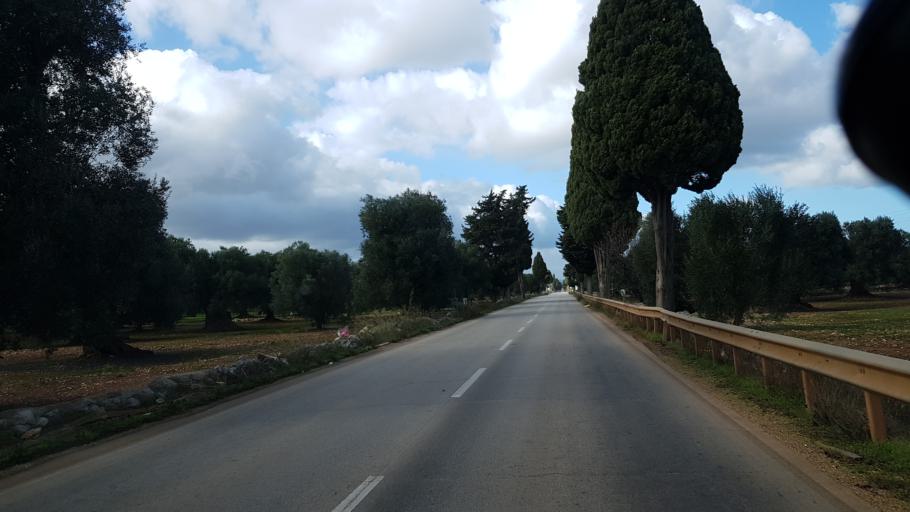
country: IT
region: Apulia
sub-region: Provincia di Brindisi
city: Montalbano
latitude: 40.7707
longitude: 17.5063
